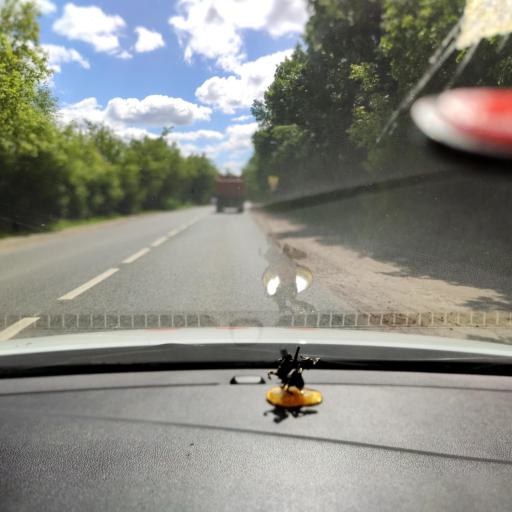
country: RU
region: Tatarstan
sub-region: Zelenodol'skiy Rayon
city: Vasil'yevo
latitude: 55.8474
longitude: 48.6772
